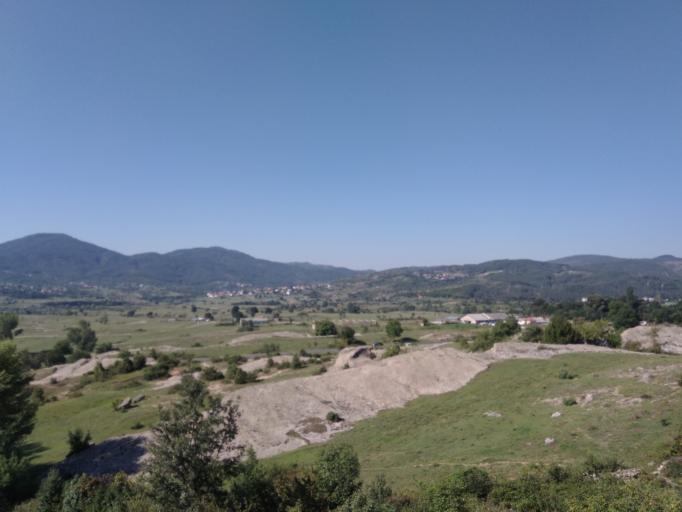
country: BG
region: Smolyan
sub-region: Obshtina Zlatograd
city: Zlatograd
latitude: 41.3820
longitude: 25.2236
